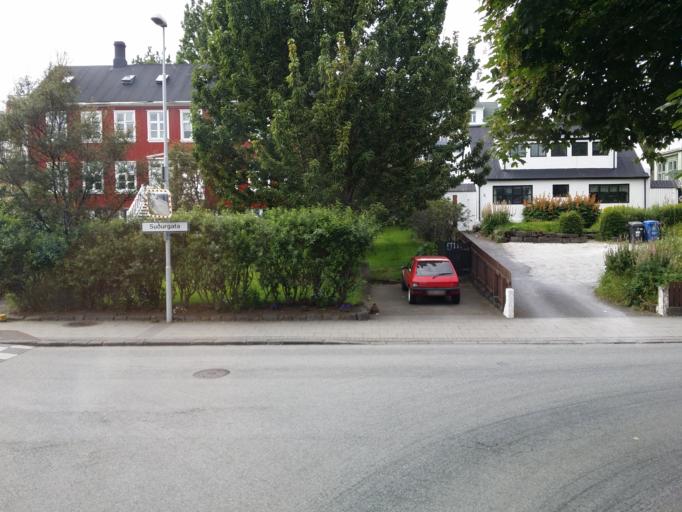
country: IS
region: Capital Region
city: Kopavogur
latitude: 64.1467
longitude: -21.9433
